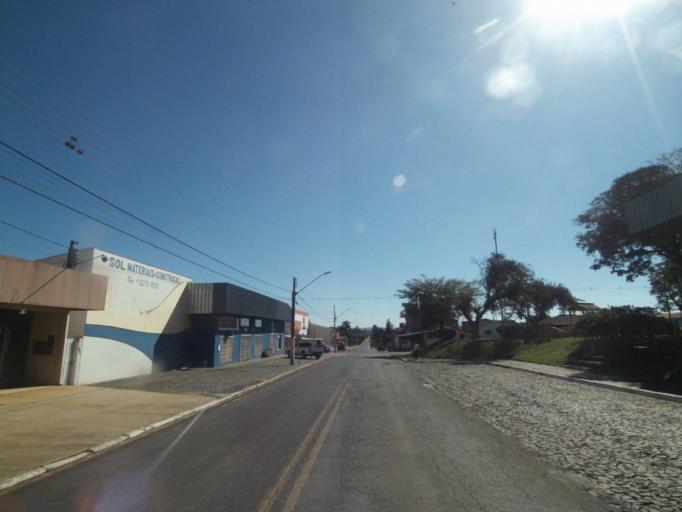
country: BR
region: Parana
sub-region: Tibagi
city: Tibagi
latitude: -24.5213
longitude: -50.4063
